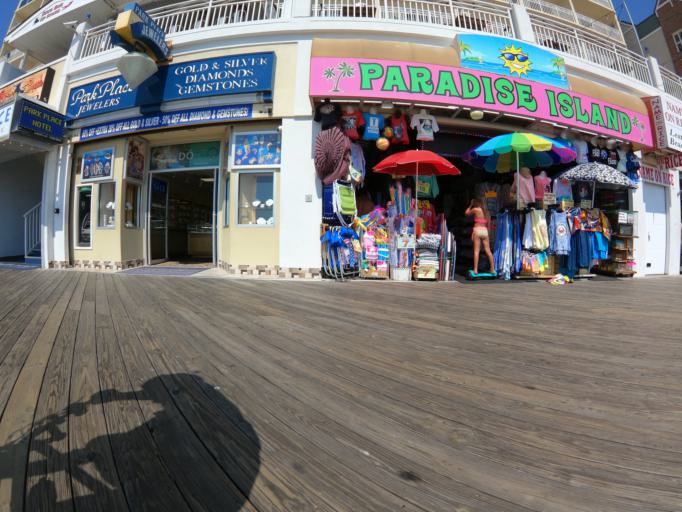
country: US
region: Maryland
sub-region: Worcester County
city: Ocean City
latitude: 38.3339
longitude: -75.0836
